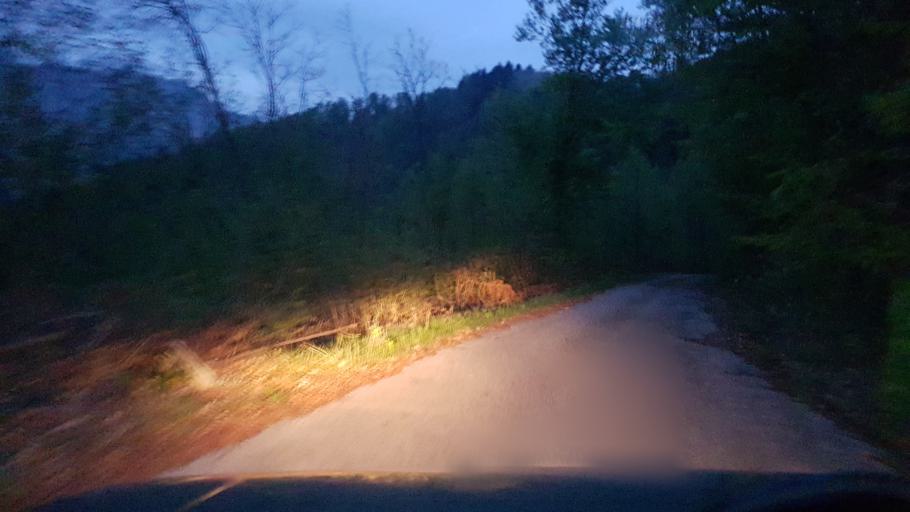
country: IT
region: Friuli Venezia Giulia
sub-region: Provincia di Udine
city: Taipana
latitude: 46.2436
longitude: 13.3555
